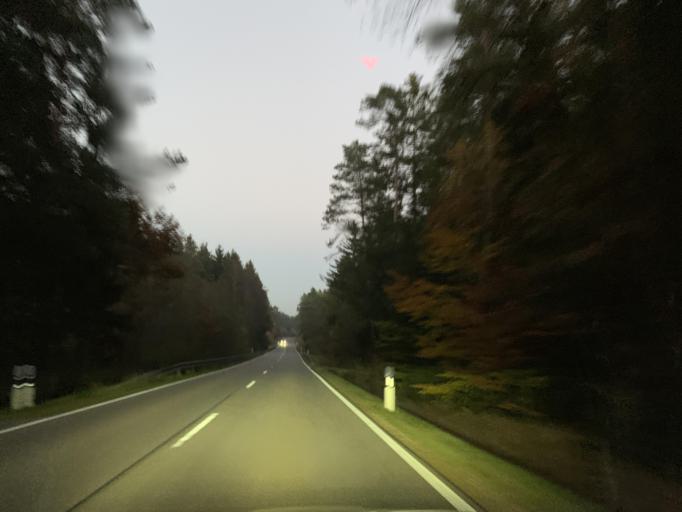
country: DE
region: Bavaria
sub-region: Upper Palatinate
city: Brunn
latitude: 49.2425
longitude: 12.2292
